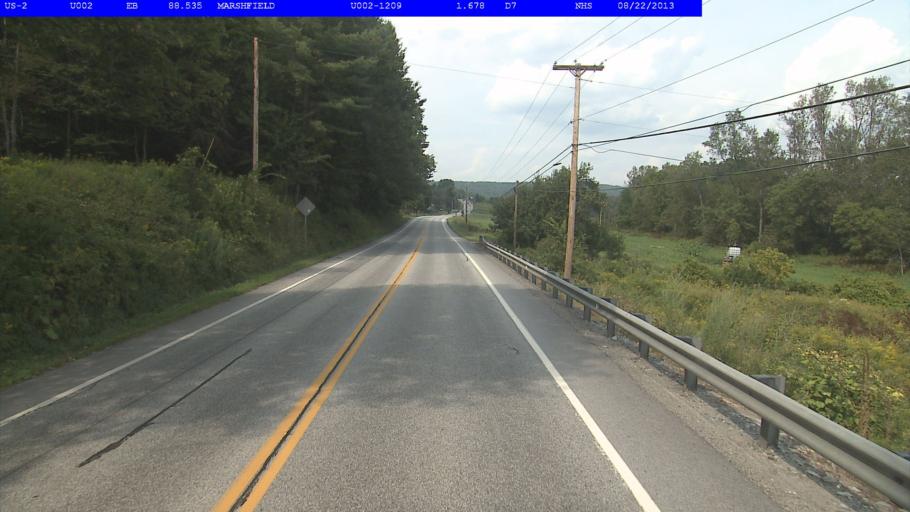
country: US
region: Vermont
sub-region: Washington County
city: Barre
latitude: 44.2951
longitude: -72.3981
